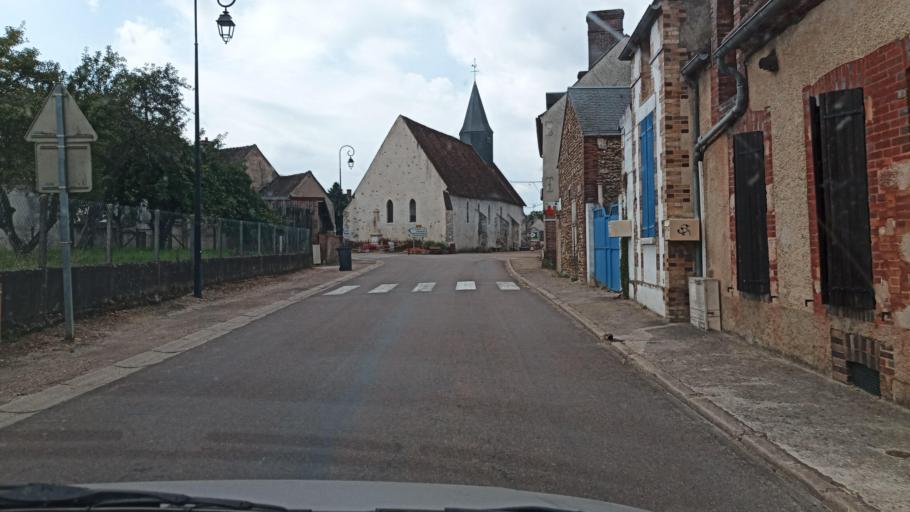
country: FR
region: Bourgogne
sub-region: Departement de l'Yonne
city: Egriselles-le-Bocage
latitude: 48.0237
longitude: 3.1761
